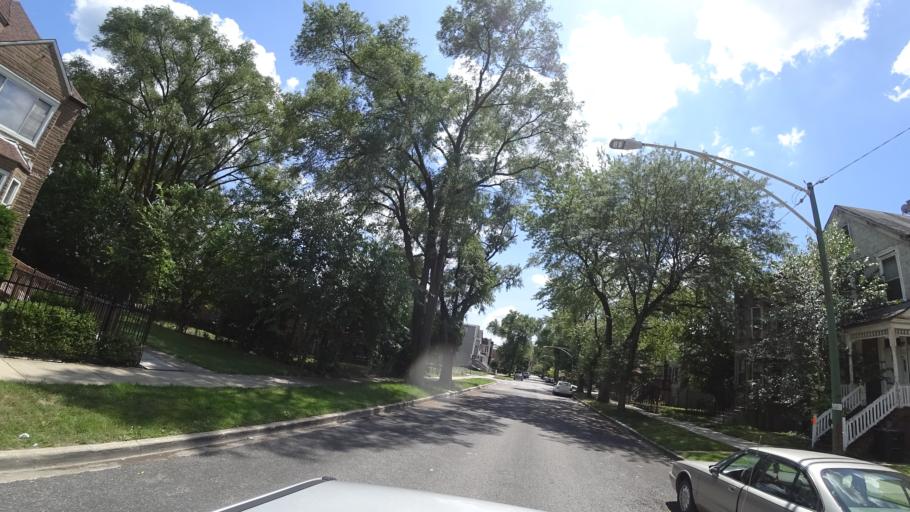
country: US
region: Illinois
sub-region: Cook County
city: Chicago
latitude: 41.7718
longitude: -87.6082
